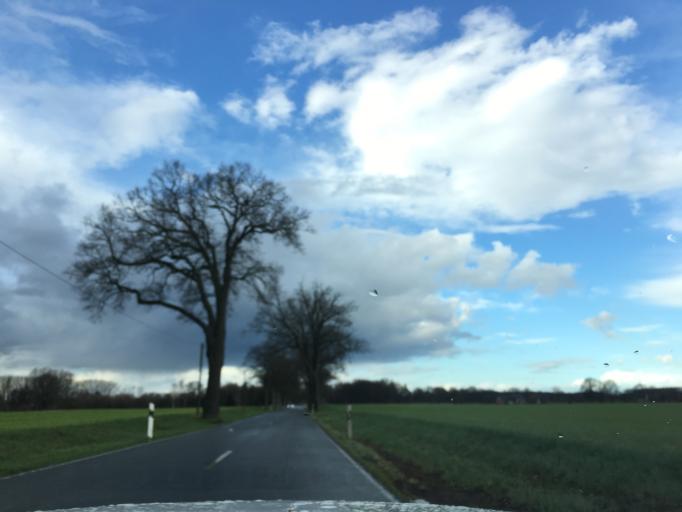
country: DE
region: North Rhine-Westphalia
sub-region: Regierungsbezirk Munster
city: Isselburg
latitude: 51.7968
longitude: 6.4792
